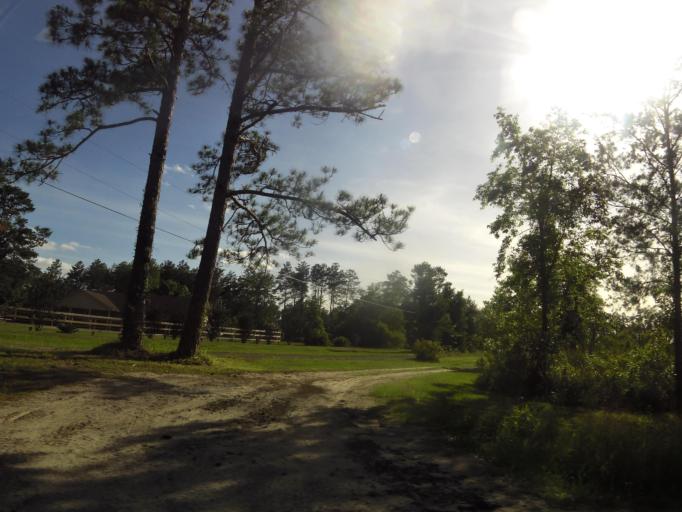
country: US
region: Florida
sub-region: Nassau County
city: Nassau Village-Ratliff
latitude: 30.4749
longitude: -81.8421
